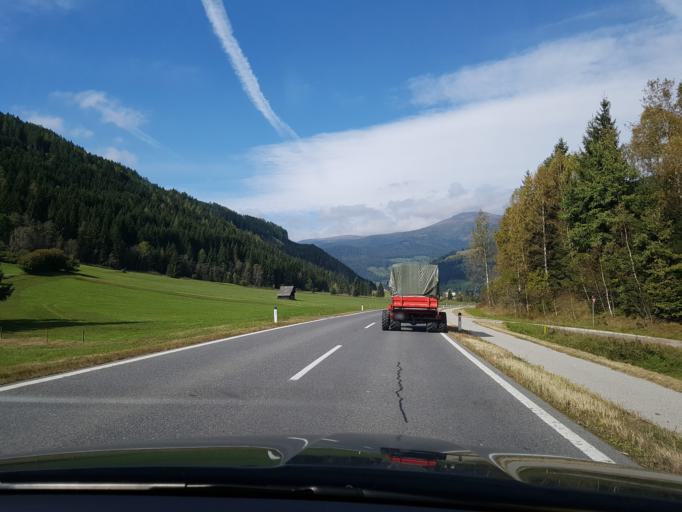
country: AT
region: Carinthia
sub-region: Politischer Bezirk Feldkirchen
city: Gnesau
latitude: 46.7989
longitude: 13.9027
